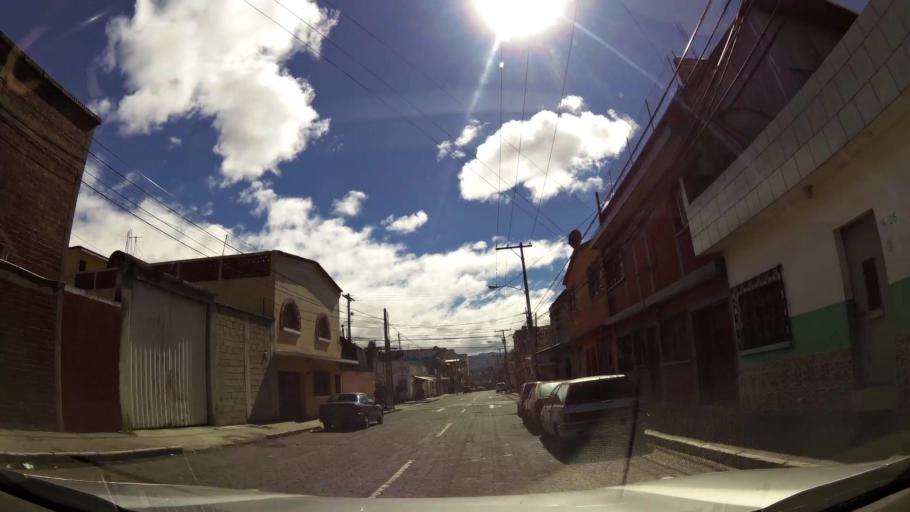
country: GT
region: Guatemala
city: Guatemala City
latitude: 14.6079
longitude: -90.5284
